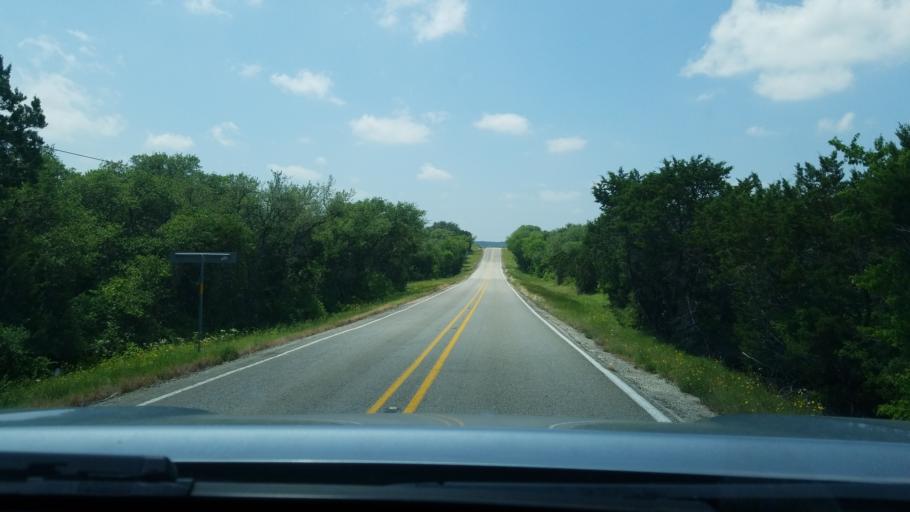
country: US
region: Texas
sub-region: Hays County
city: Woodcreek
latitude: 30.0982
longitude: -98.2411
